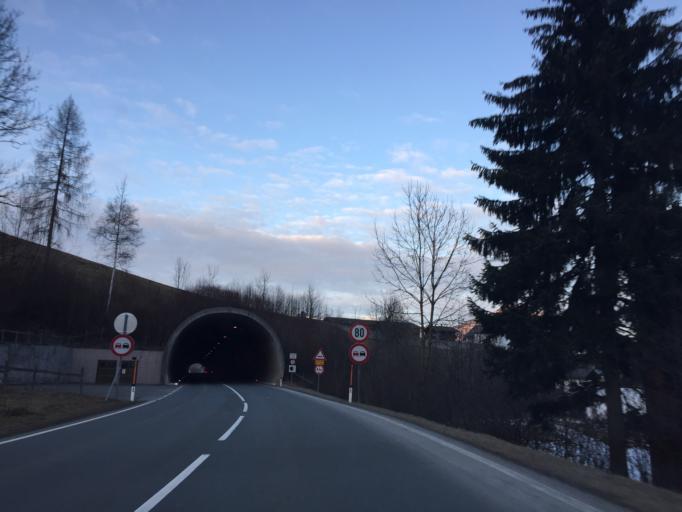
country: AT
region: Salzburg
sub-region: Politischer Bezirk Zell am See
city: Kaprun
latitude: 47.2709
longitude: 12.7531
